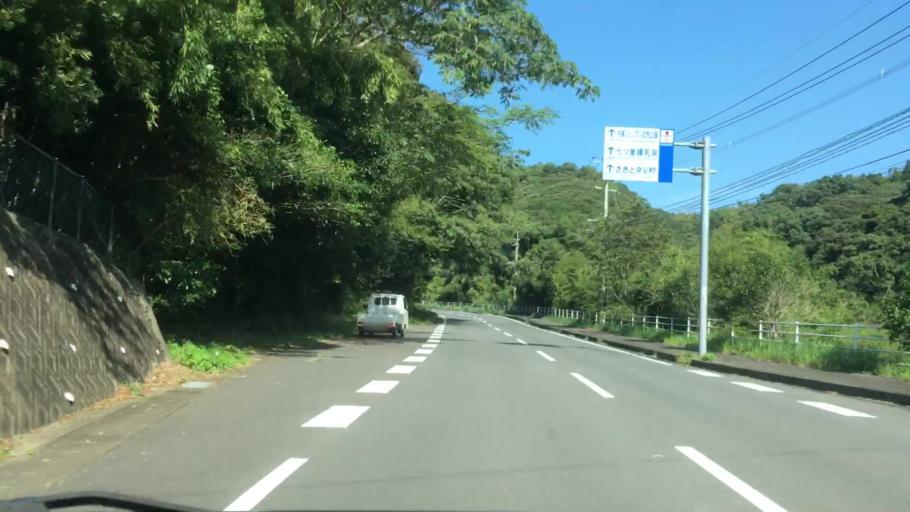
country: JP
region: Nagasaki
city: Sasebo
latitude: 33.0030
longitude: 129.6607
